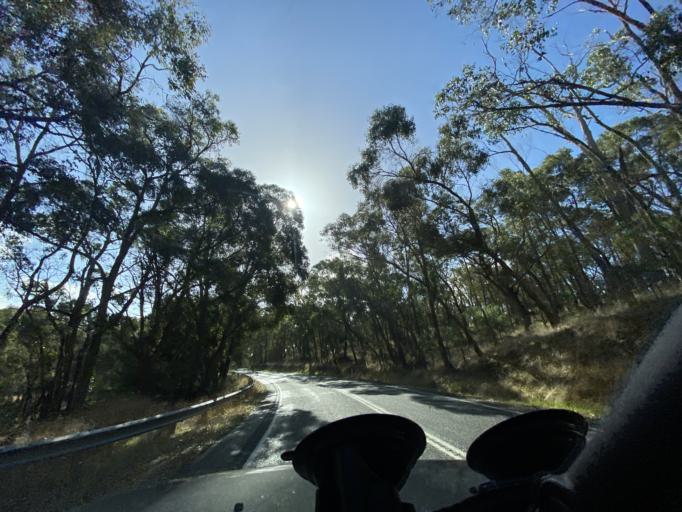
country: AU
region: Victoria
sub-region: Murrindindi
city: Kinglake West
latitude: -37.3010
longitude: 145.3694
